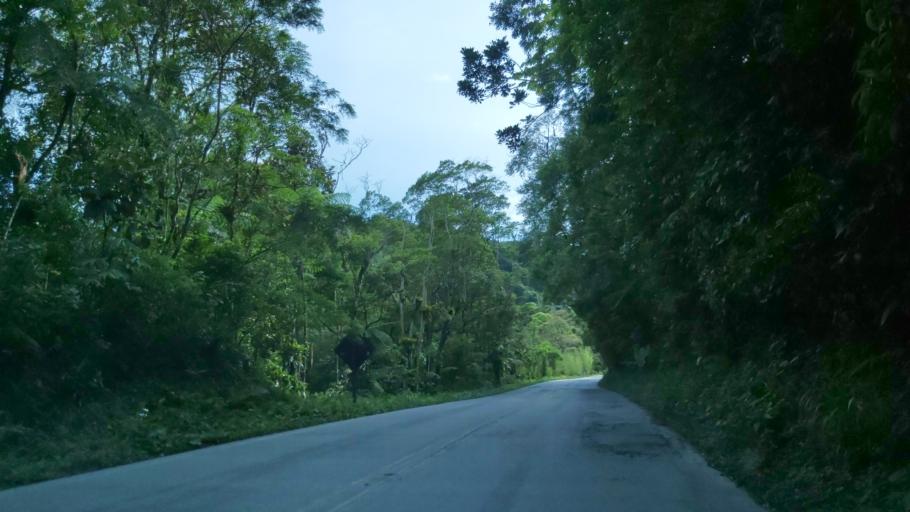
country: BR
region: Sao Paulo
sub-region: Miracatu
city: Miracatu
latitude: -24.0358
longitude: -47.5663
